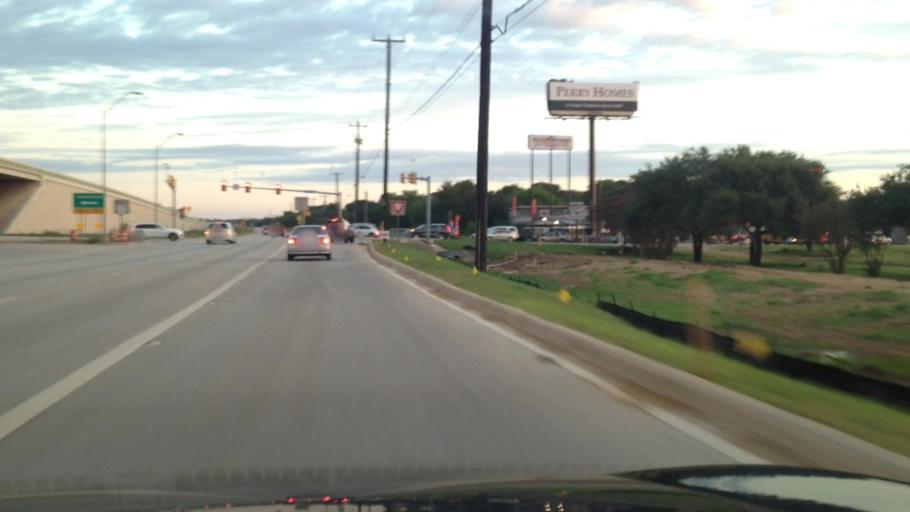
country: US
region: Texas
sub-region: Bexar County
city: Cross Mountain
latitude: 29.6245
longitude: -98.6091
